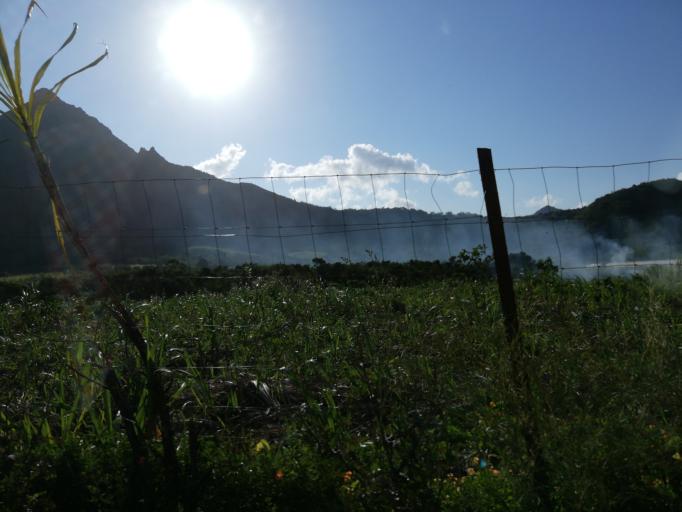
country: MU
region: Moka
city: Saint Pierre
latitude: -20.2108
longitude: 57.5250
